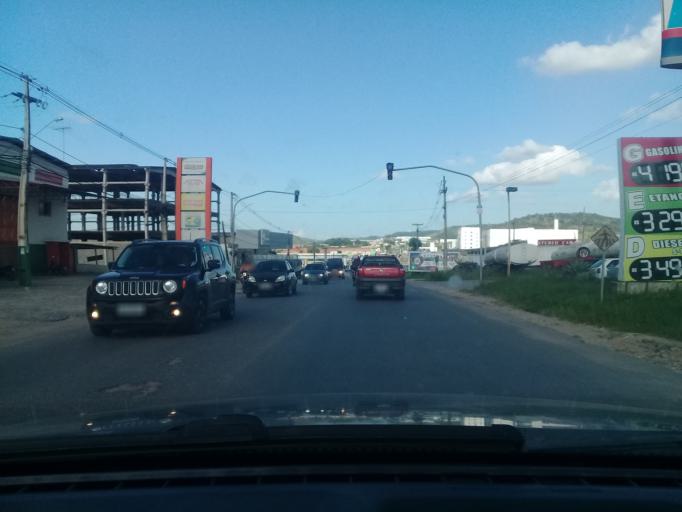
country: BR
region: Pernambuco
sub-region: Vitoria De Santo Antao
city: Vitoria de Santo Antao
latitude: -8.1148
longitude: -35.2763
